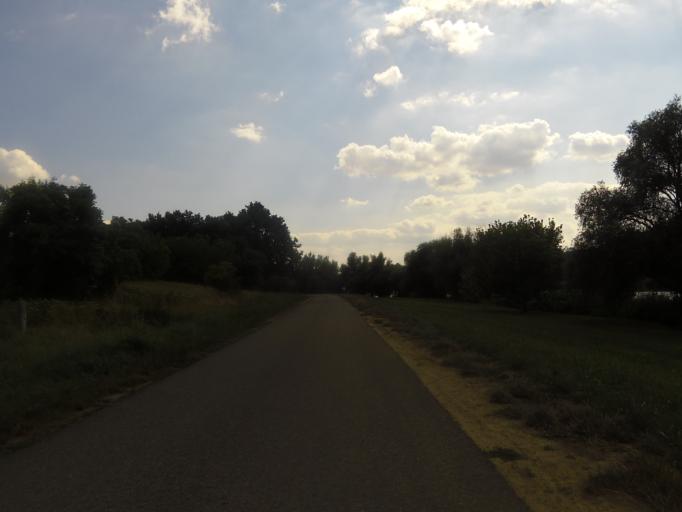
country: HU
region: Jasz-Nagykun-Szolnok
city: Tiszafured
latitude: 47.6190
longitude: 20.7267
